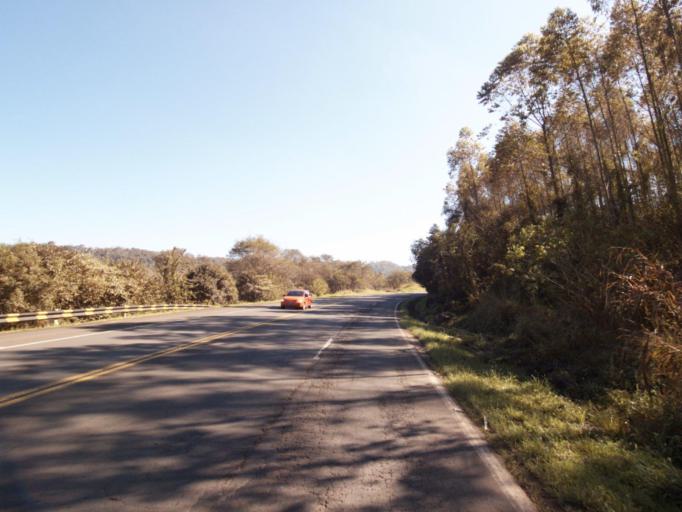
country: BR
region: Rio Grande do Sul
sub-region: Frederico Westphalen
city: Frederico Westphalen
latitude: -27.0770
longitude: -53.2305
